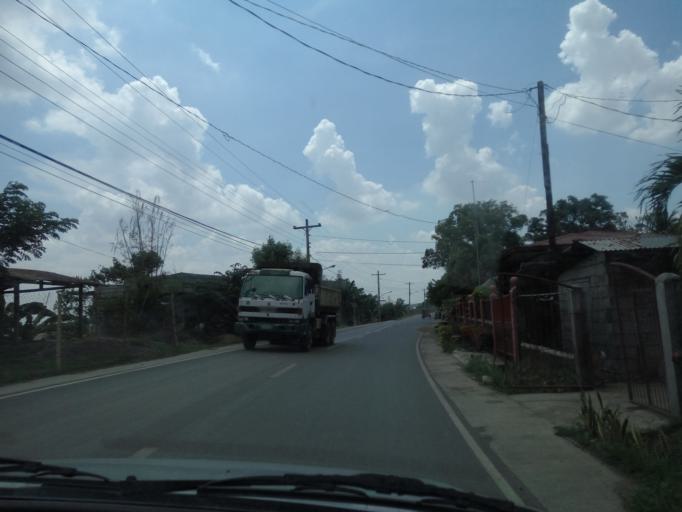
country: PH
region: Central Luzon
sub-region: Province of Nueva Ecija
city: Rizal
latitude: 15.7138
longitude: 121.0992
